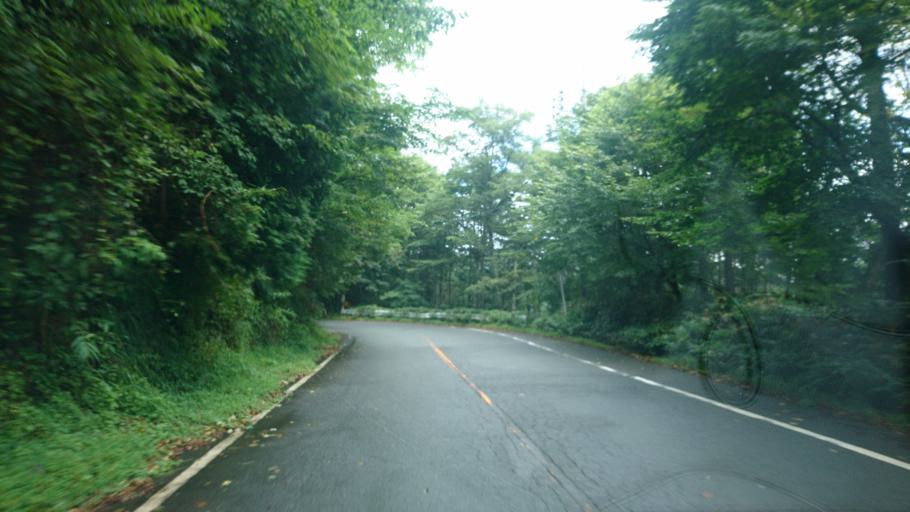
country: JP
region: Gunma
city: Omamacho-omama
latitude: 36.5756
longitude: 139.2353
